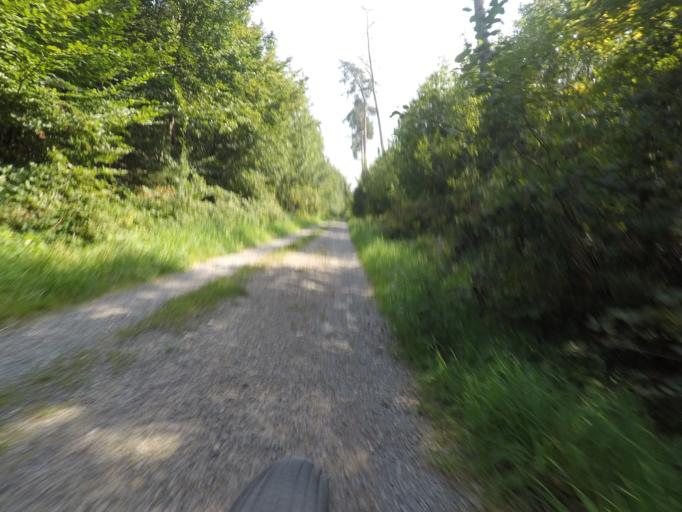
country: DE
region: Baden-Wuerttemberg
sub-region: Regierungsbezirk Stuttgart
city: Steinenbronn
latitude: 48.6740
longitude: 9.1103
